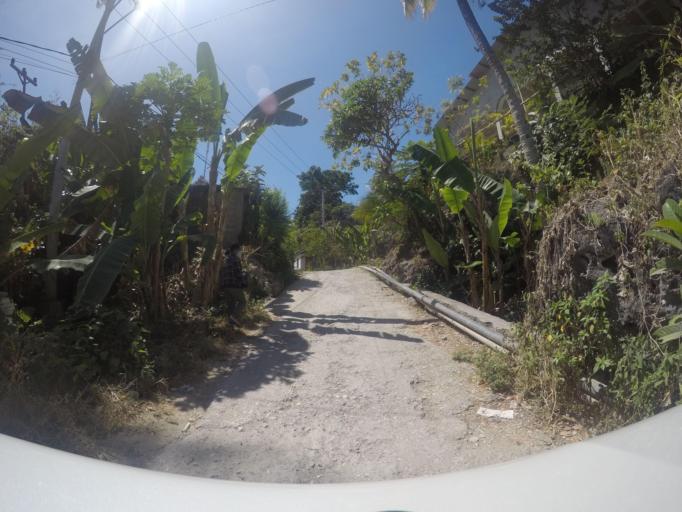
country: TL
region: Baucau
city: Baucau
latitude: -8.4644
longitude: 126.4533
